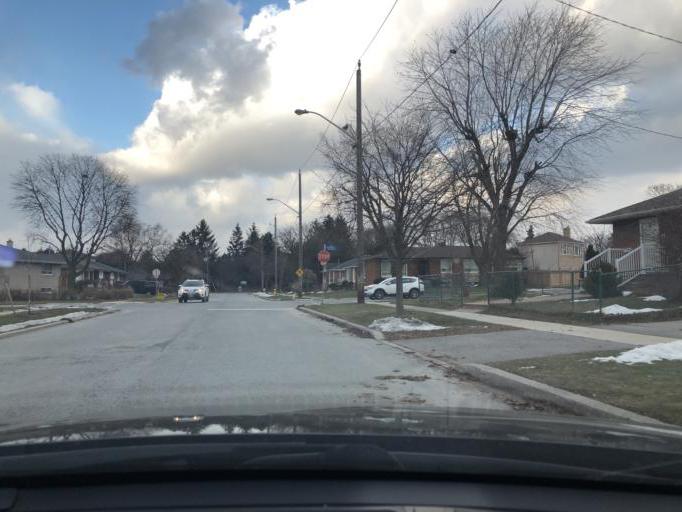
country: CA
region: Ontario
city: Scarborough
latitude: 43.7753
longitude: -79.2914
